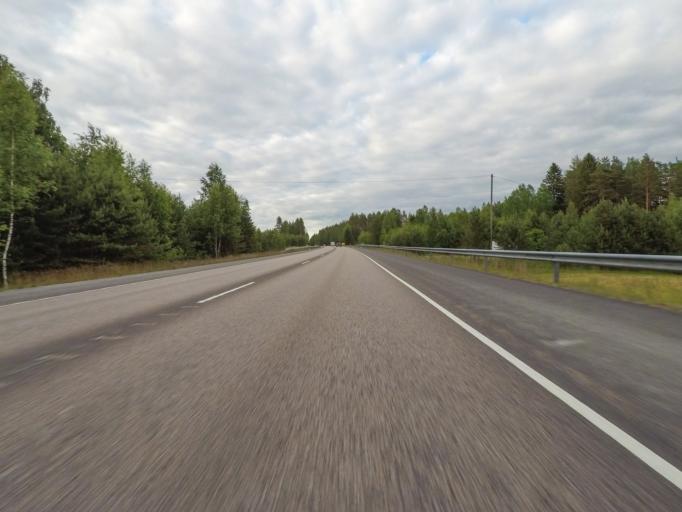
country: FI
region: Paijanne Tavastia
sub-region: Lahti
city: Heinola
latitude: 61.3234
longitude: 26.1541
